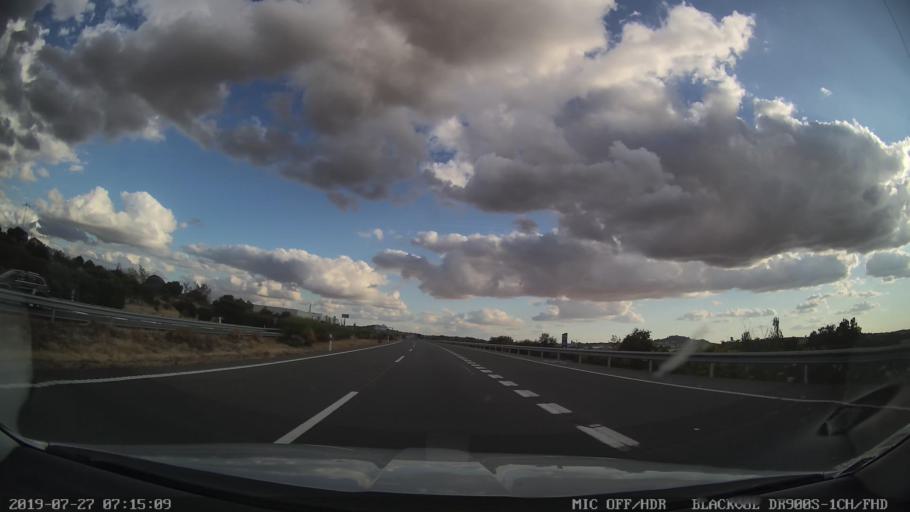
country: ES
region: Extremadura
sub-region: Provincia de Caceres
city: Trujillo
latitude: 39.4811
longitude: -5.8512
